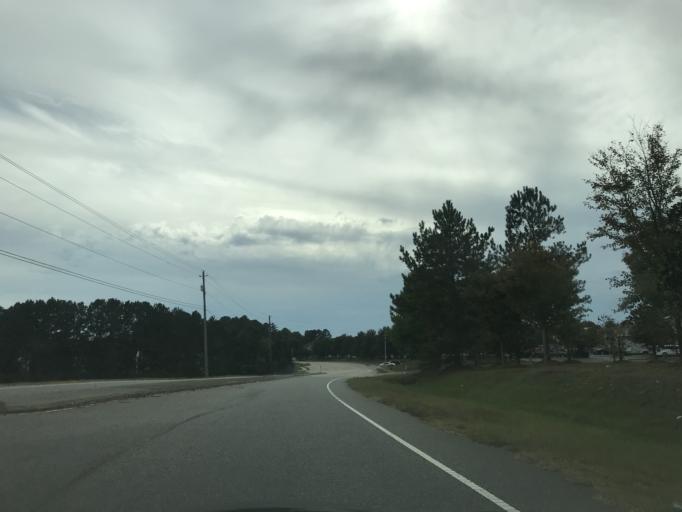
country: US
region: North Carolina
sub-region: Wake County
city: Rolesville
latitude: 35.8945
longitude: -78.5068
